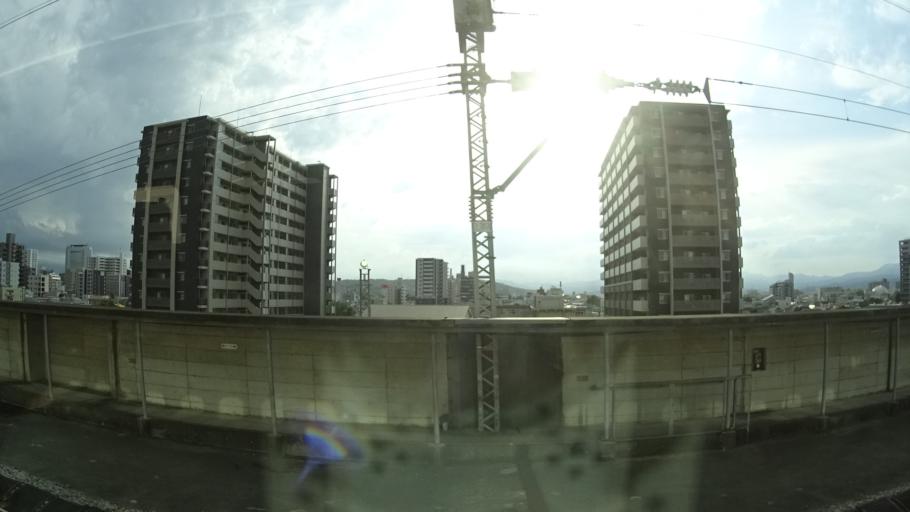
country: JP
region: Gunma
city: Takasaki
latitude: 36.3305
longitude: 139.0121
